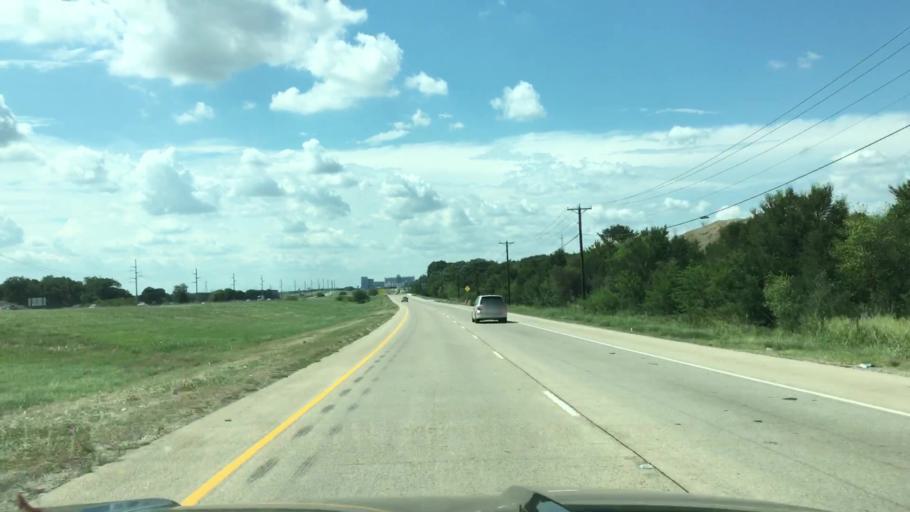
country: US
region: Texas
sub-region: Denton County
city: Roanoke
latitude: 33.0192
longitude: -97.2432
